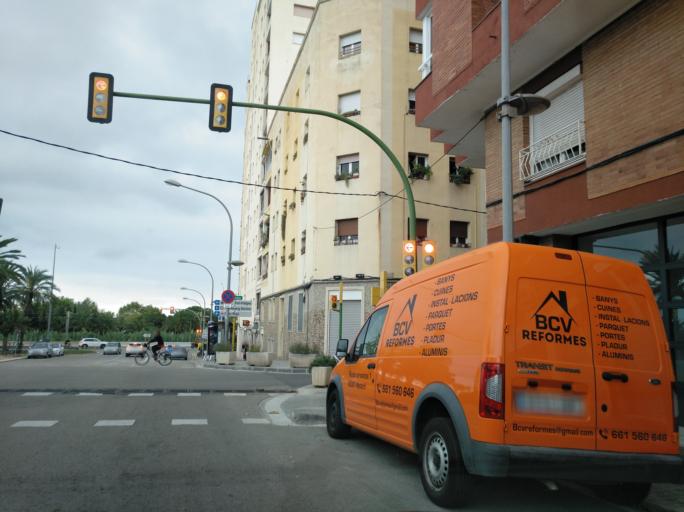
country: ES
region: Catalonia
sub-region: Provincia de Barcelona
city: Mataro
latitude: 41.5416
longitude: 2.4558
